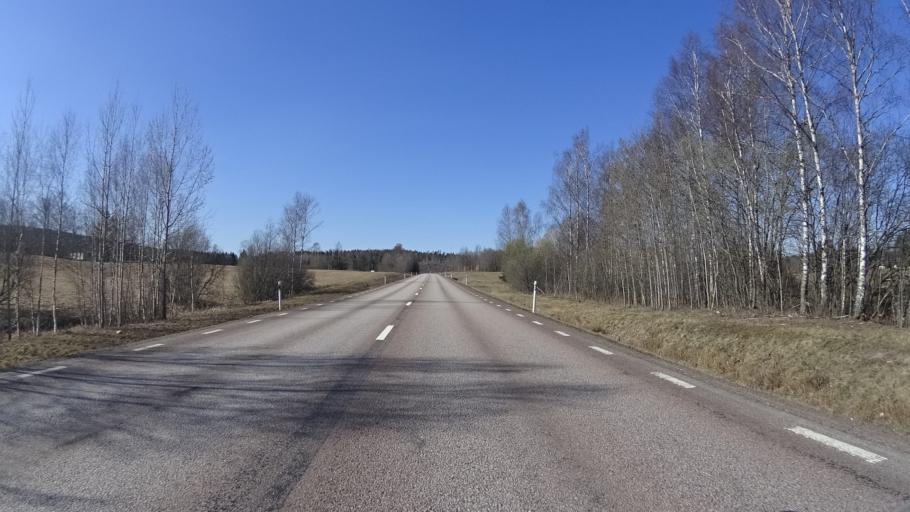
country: SE
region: Vaermland
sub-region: Karlstads Kommun
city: Edsvalla
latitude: 59.5187
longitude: 13.1647
